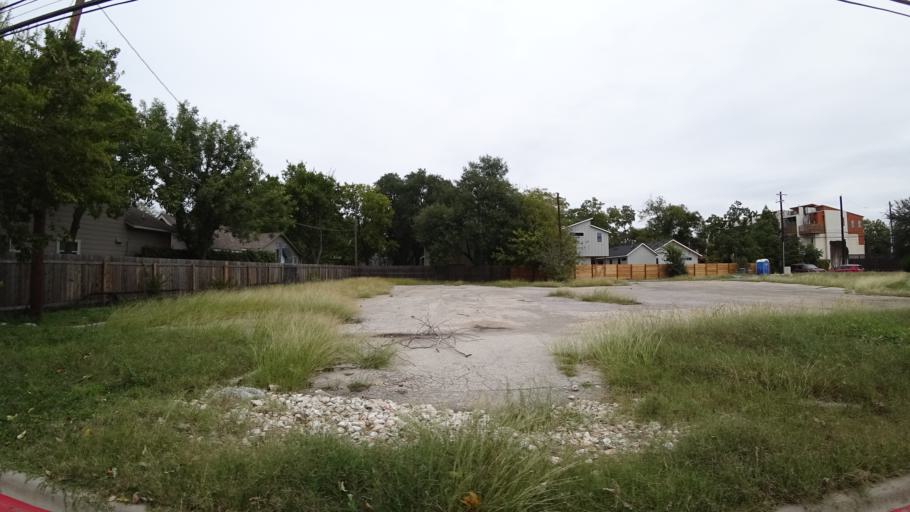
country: US
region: Texas
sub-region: Travis County
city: Austin
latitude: 30.2936
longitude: -97.7223
